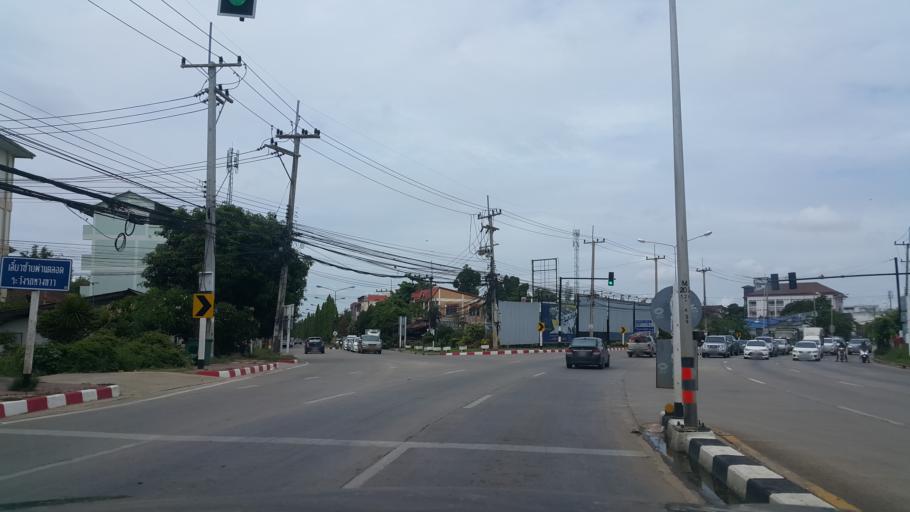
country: TH
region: Phitsanulok
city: Phitsanulok
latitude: 16.8211
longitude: 100.2458
